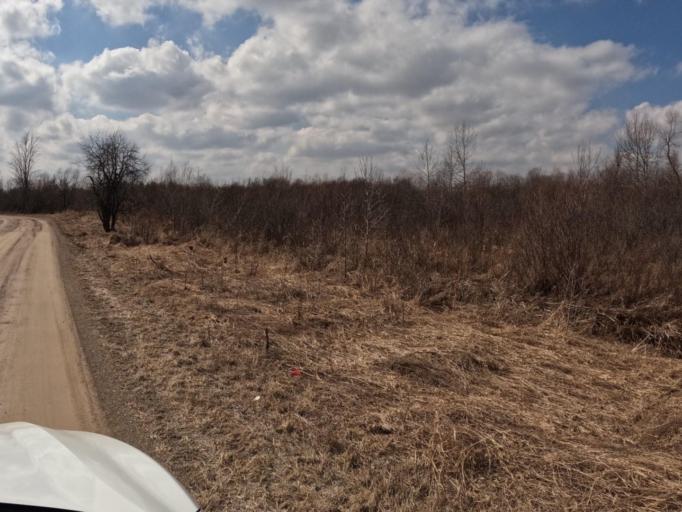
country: CA
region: Ontario
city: Shelburne
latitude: 43.9686
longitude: -80.2739
